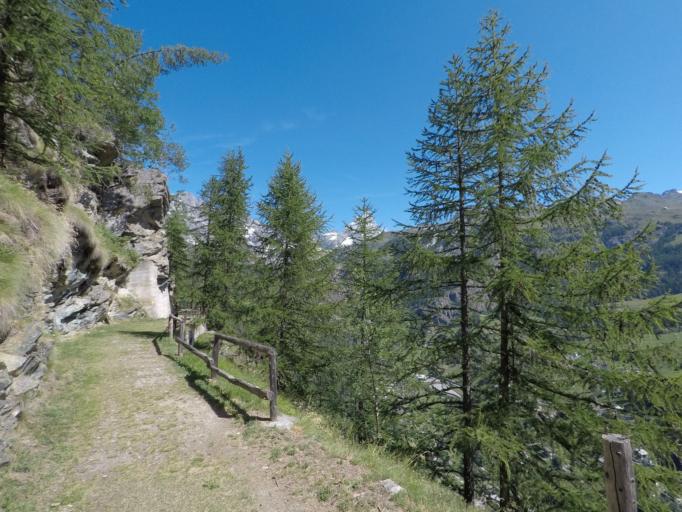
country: IT
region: Aosta Valley
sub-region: Valle d'Aosta
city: Valtournenche
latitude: 45.8794
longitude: 7.6182
